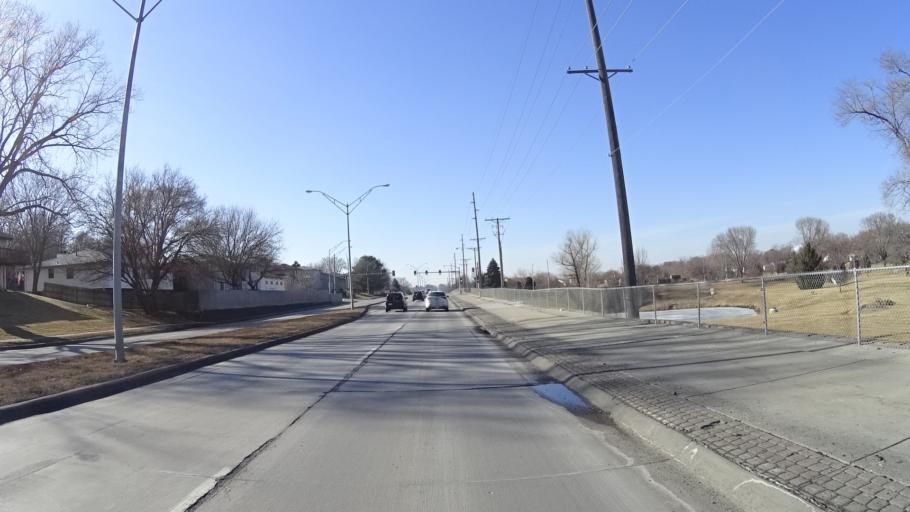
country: US
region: Nebraska
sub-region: Douglas County
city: Bennington
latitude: 41.3067
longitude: -96.0875
